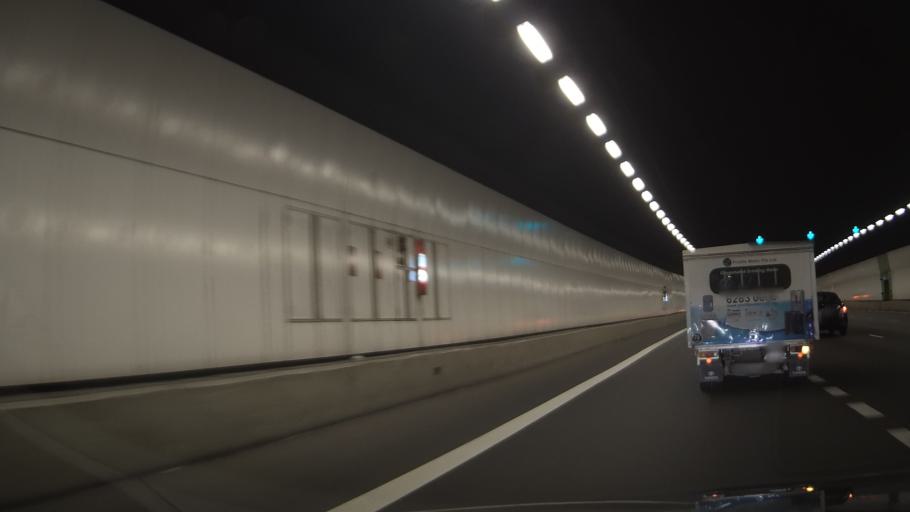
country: SG
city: Singapore
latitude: 1.3199
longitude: 103.8839
